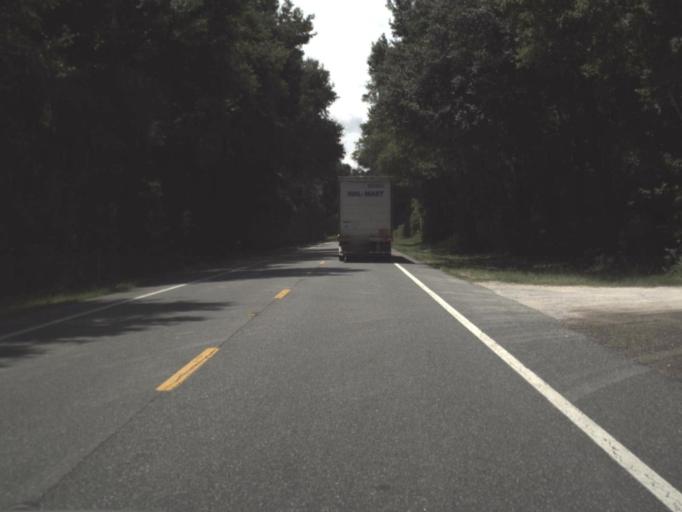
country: US
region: Florida
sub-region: Alachua County
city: Newberry
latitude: 29.5946
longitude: -82.5669
